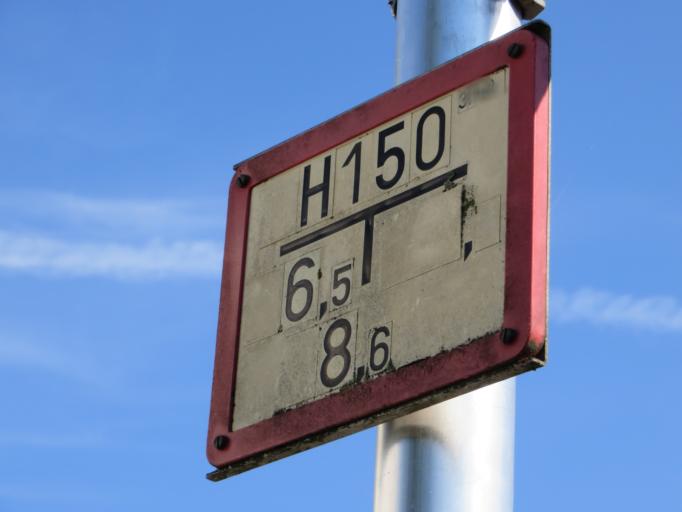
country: DE
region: North Rhine-Westphalia
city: Witten
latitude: 51.4485
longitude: 7.3240
